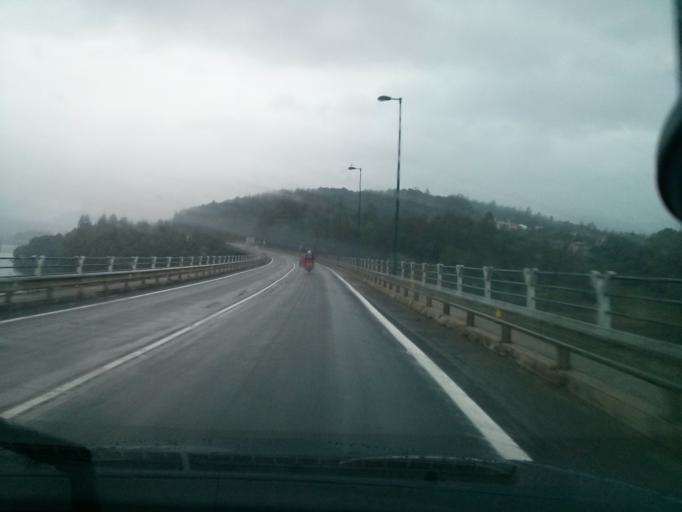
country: ES
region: Galicia
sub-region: Provincia da Coruna
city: Noia
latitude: 42.8147
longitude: -8.8852
